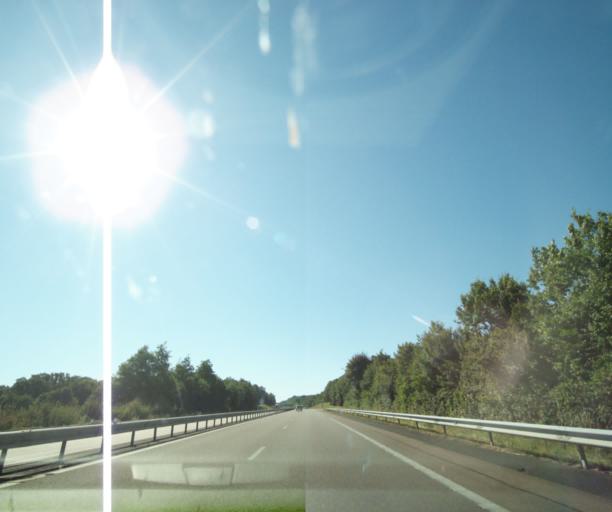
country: FR
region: Champagne-Ardenne
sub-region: Departement de la Haute-Marne
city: Chateauvillain
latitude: 48.0555
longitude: 4.9595
